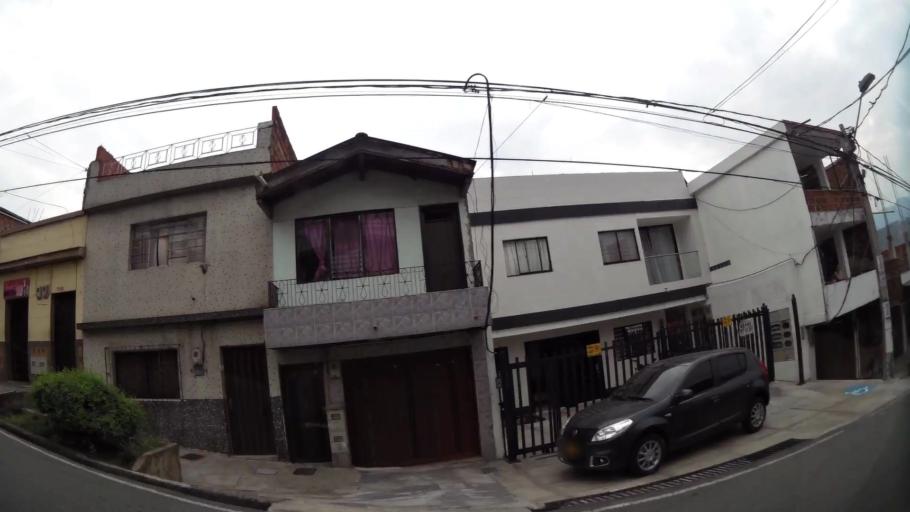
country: CO
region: Antioquia
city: Medellin
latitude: 6.2721
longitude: -75.5600
